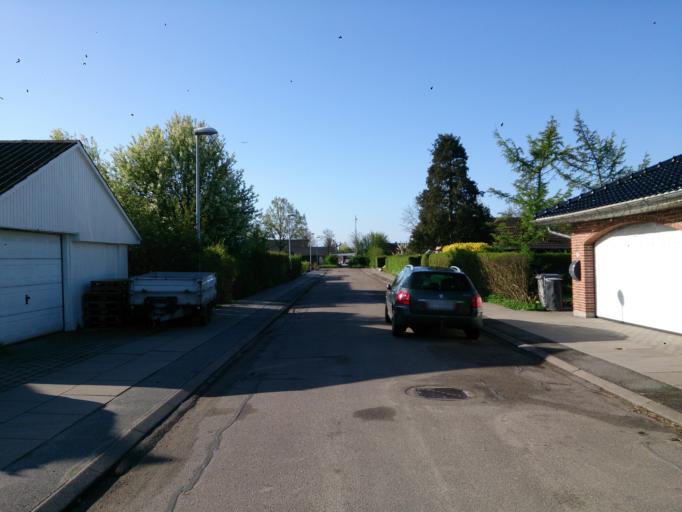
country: DK
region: Capital Region
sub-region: Tarnby Kommune
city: Tarnby
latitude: 55.6137
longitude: 12.5818
